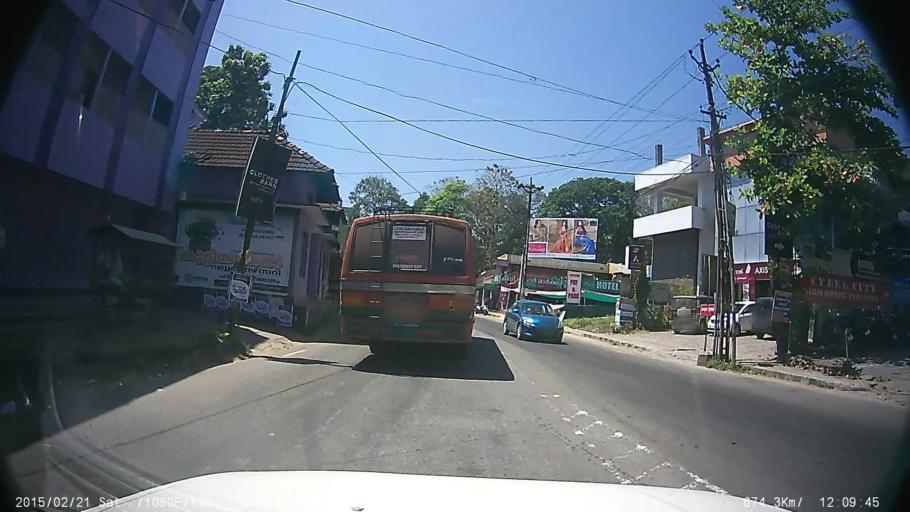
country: IN
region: Kerala
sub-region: Kottayam
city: Lalam
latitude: 9.7084
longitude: 76.6726
